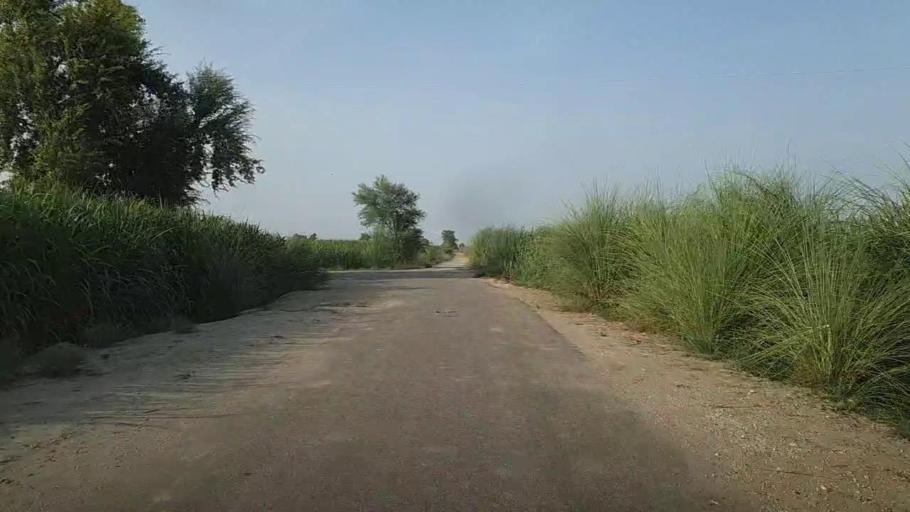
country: PK
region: Sindh
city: Ubauro
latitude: 28.0994
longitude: 69.8235
